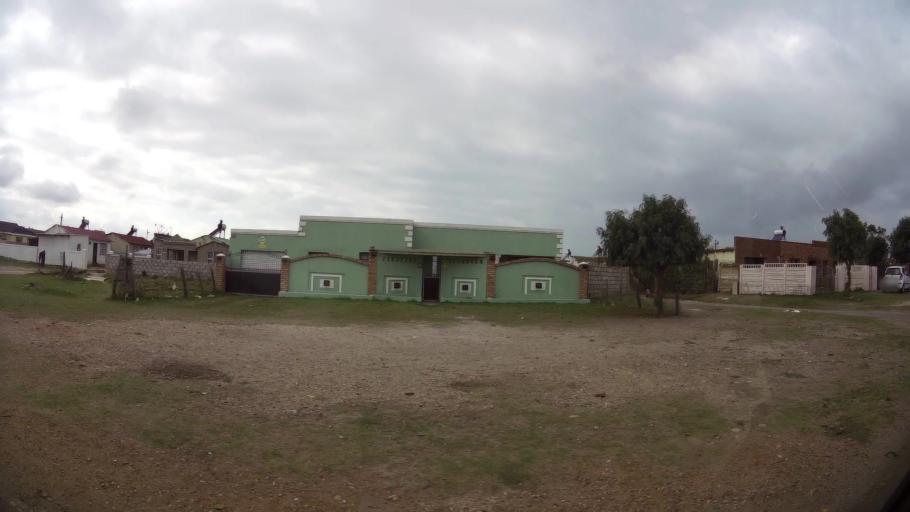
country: ZA
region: Eastern Cape
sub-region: Nelson Mandela Bay Metropolitan Municipality
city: Port Elizabeth
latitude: -33.8830
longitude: 25.6032
